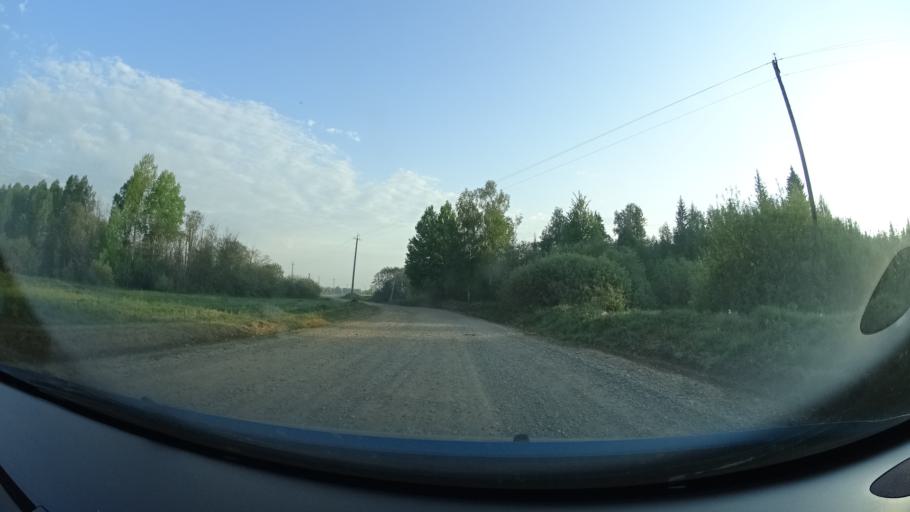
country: RU
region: Perm
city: Barda
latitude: 56.6950
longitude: 55.6824
